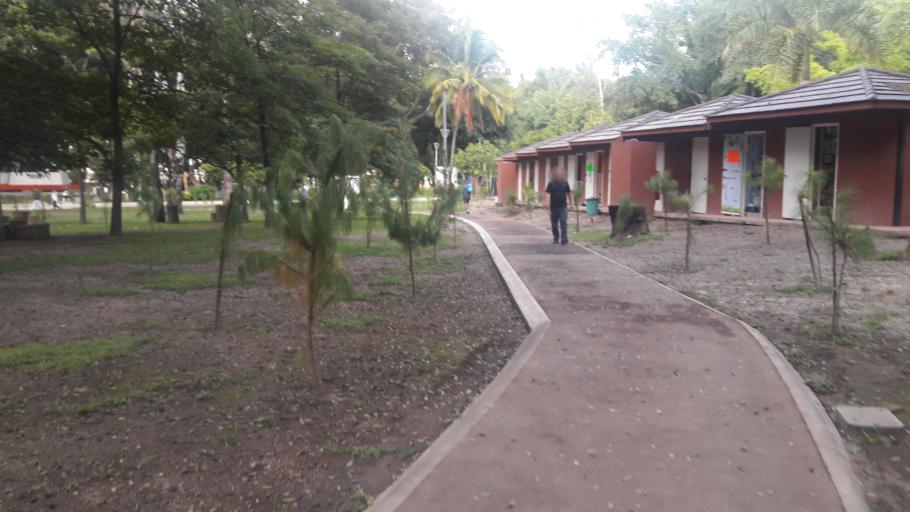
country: MX
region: Nayarit
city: Tepic
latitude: 21.5036
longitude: -104.8998
